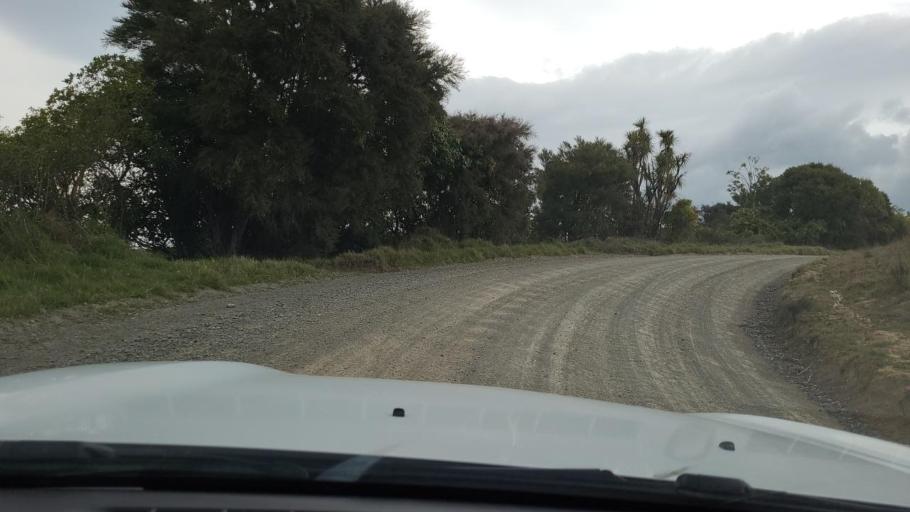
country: NZ
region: Hawke's Bay
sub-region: Napier City
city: Napier
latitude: -39.3094
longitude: 176.8278
